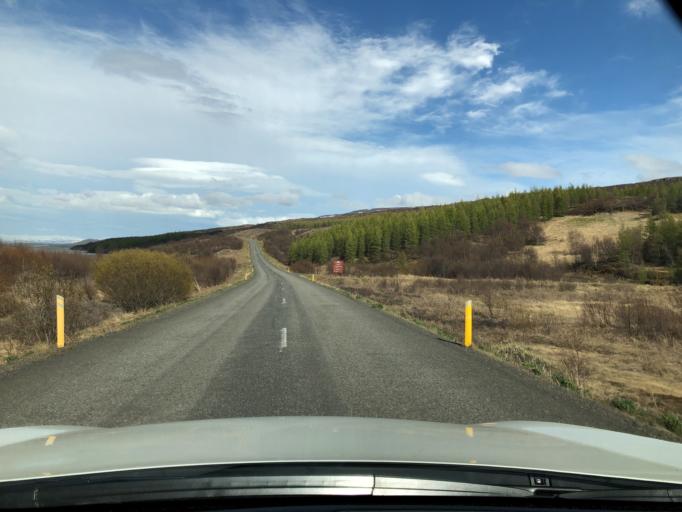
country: IS
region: East
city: Egilsstadir
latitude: 65.0697
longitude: -14.8321
